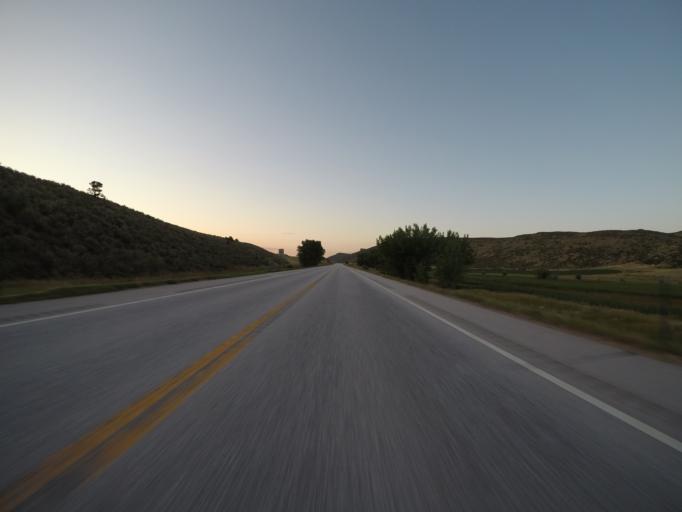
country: US
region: Colorado
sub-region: Larimer County
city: Laporte
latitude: 40.6823
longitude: -105.1776
